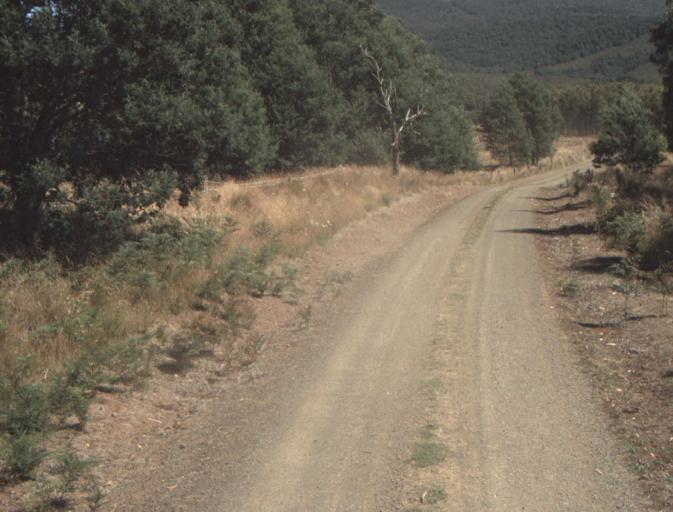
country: AU
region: Tasmania
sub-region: Dorset
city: Scottsdale
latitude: -41.3482
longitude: 147.4534
